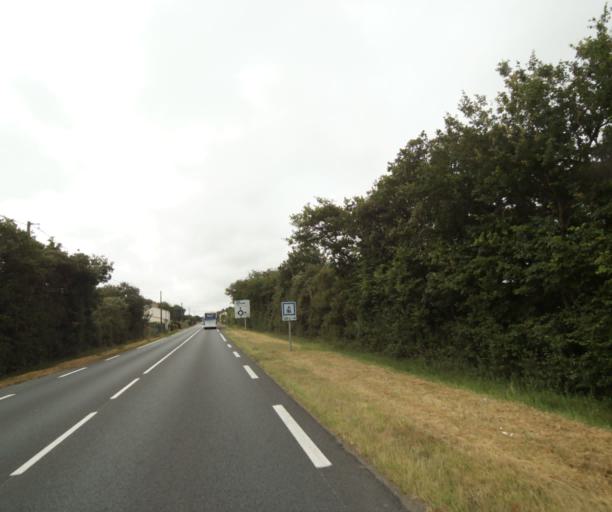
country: FR
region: Pays de la Loire
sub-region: Departement de la Vendee
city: Chateau-d'Olonne
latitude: 46.4791
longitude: -1.6916
